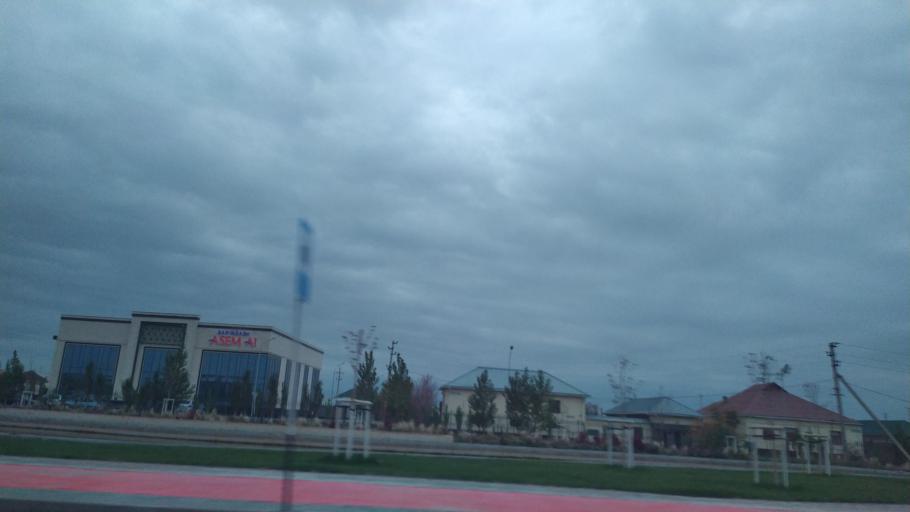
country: KZ
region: Ongtustik Qazaqstan
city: Turkestan
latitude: 43.2823
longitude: 68.3154
